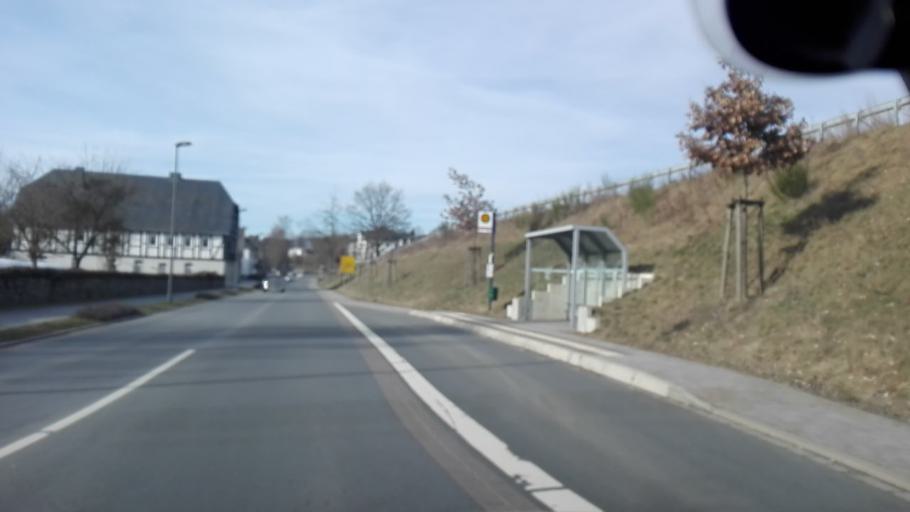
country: DE
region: North Rhine-Westphalia
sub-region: Regierungsbezirk Arnsberg
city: Bad Fredeburg
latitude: 51.1582
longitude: 8.3428
